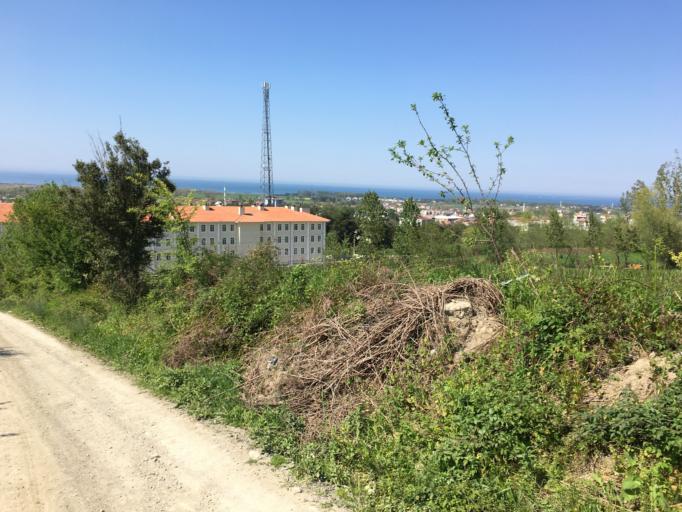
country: TR
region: Samsun
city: Alacam
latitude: 41.6069
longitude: 35.6044
